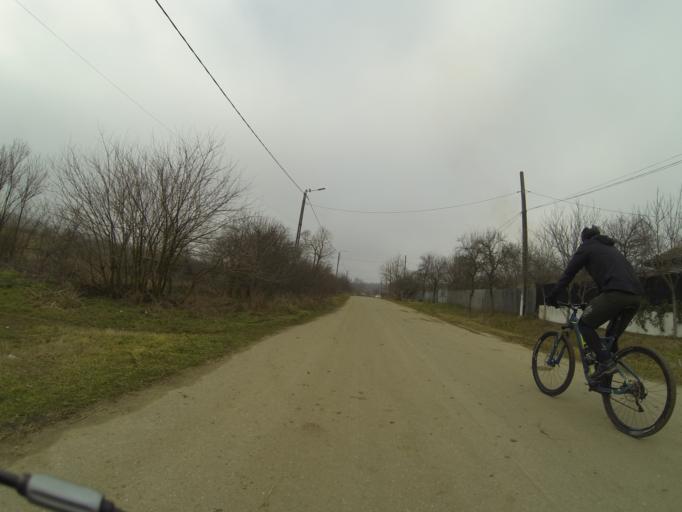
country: RO
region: Mehedinti
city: Padina Mica
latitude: 44.4899
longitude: 23.0110
